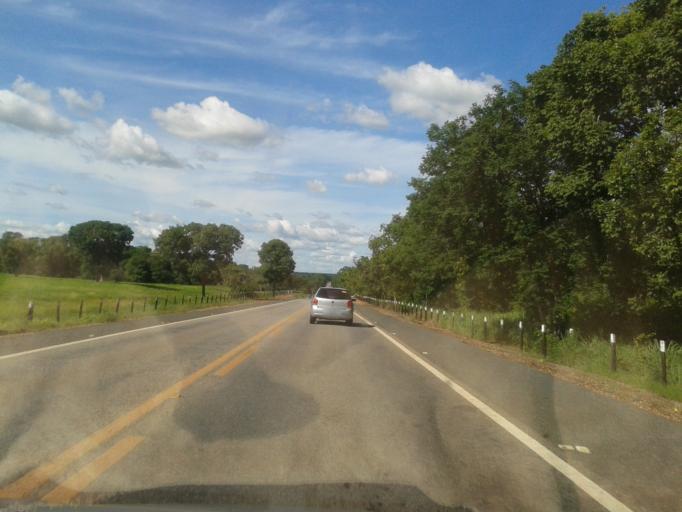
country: BR
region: Goias
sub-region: Mozarlandia
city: Mozarlandia
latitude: -15.0055
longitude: -50.5911
